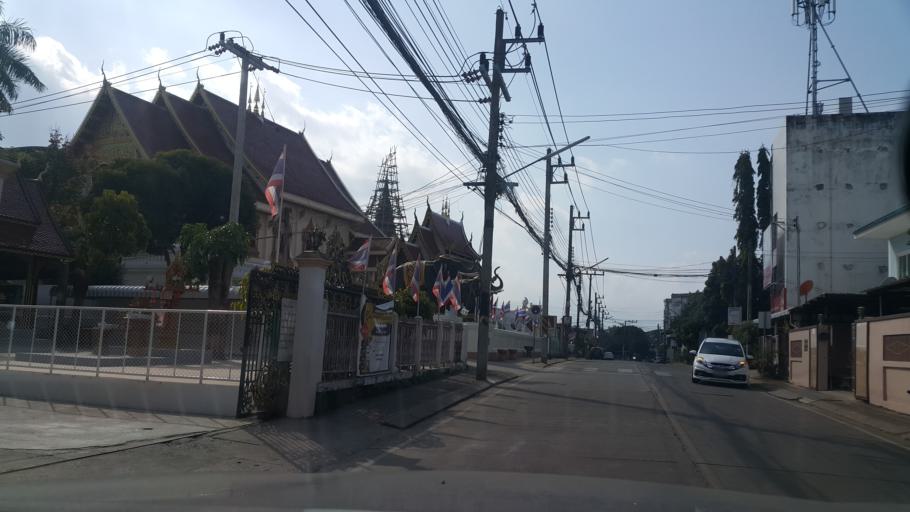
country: TH
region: Phayao
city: Phayao
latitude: 19.1651
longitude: 99.8998
